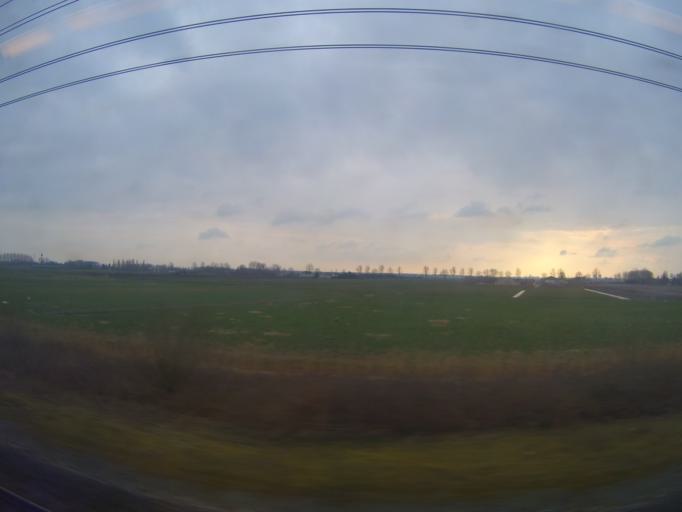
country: NL
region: South Holland
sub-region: Gemeente Waddinxveen
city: Waddinxveen
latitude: 52.0095
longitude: 4.6444
